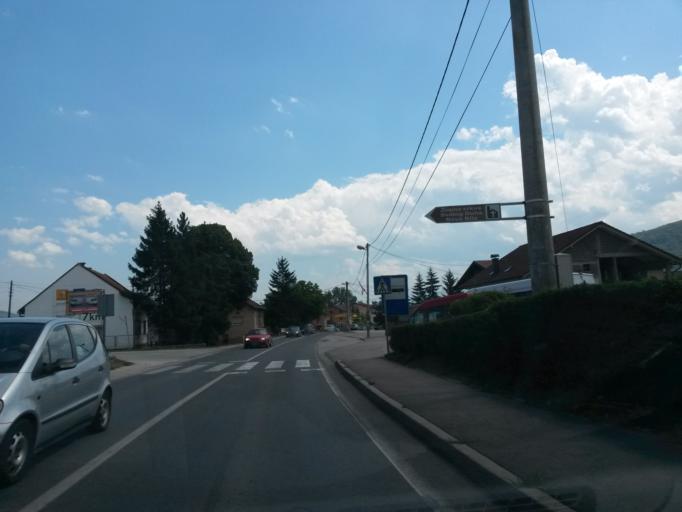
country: BA
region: Federation of Bosnia and Herzegovina
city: Travnik
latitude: 44.1982
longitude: 17.7285
